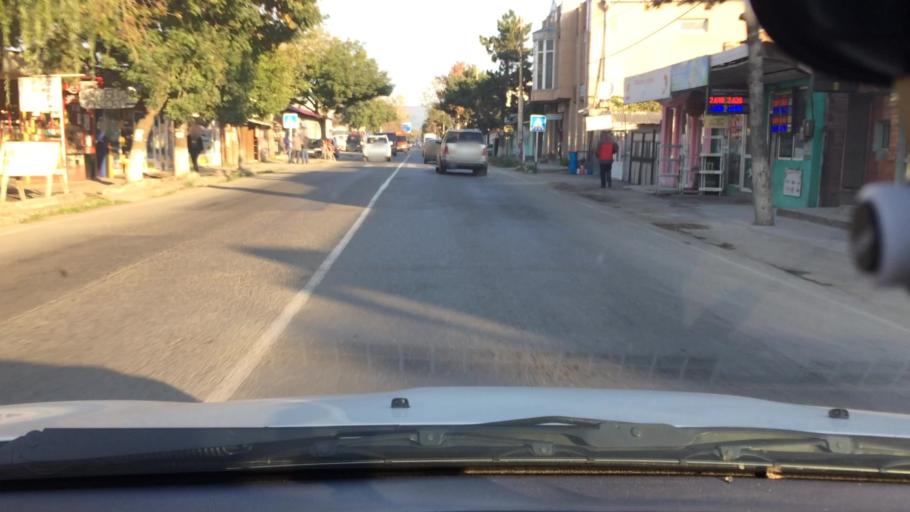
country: GE
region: Shida Kartli
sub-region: Khashuris Raioni
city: Khashuri
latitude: 41.9867
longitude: 43.5942
